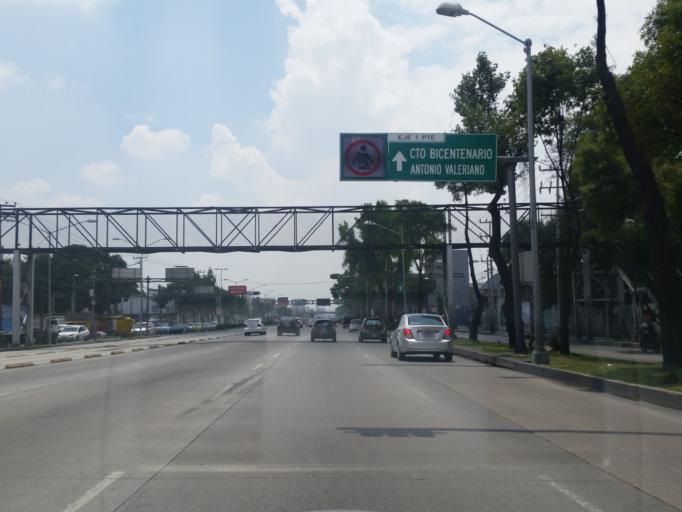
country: MX
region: Mexico
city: Colonia Lindavista
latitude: 19.4831
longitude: -99.1498
